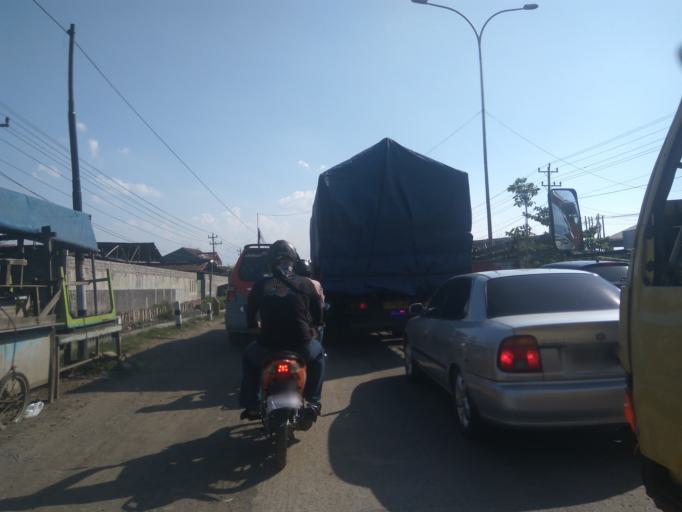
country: ID
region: Central Java
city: Semarang
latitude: -6.9535
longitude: 110.4755
